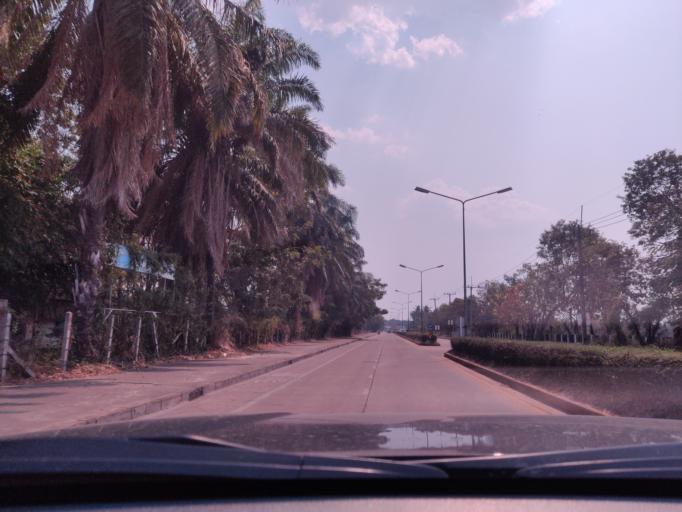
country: TH
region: Sisaket
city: Si Sa Ket
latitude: 15.1047
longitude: 104.3154
